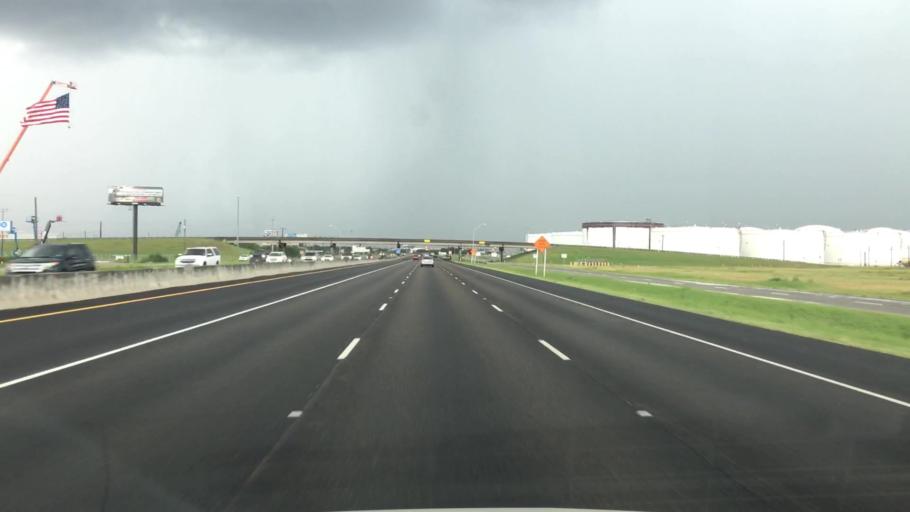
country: US
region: Texas
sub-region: Nueces County
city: Corpus Christi
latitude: 27.8101
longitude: -97.4998
